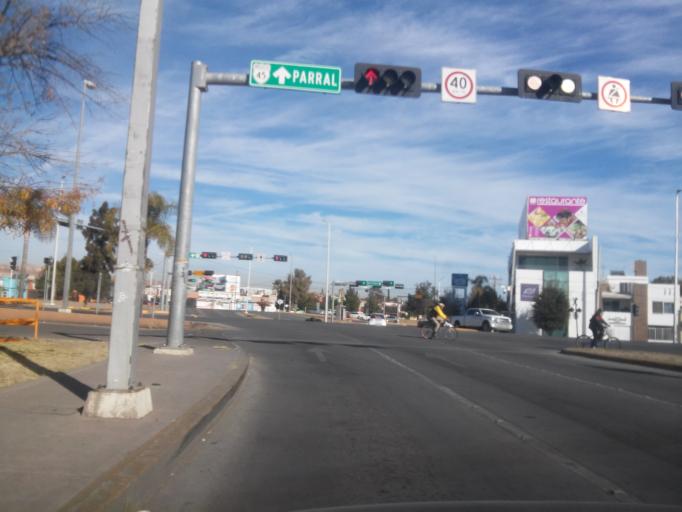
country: MX
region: Durango
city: Victoria de Durango
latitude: 24.0371
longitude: -104.6546
